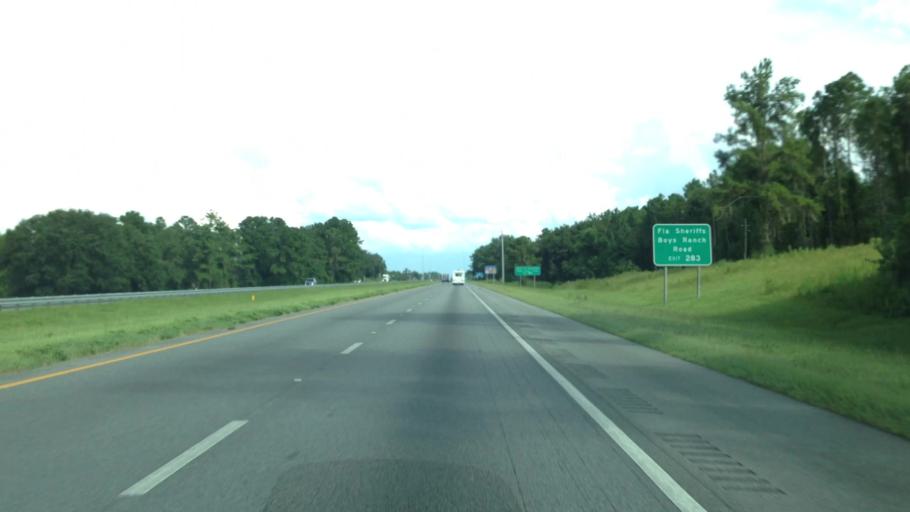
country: US
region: Florida
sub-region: Suwannee County
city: Live Oak
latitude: 30.3406
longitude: -82.9765
